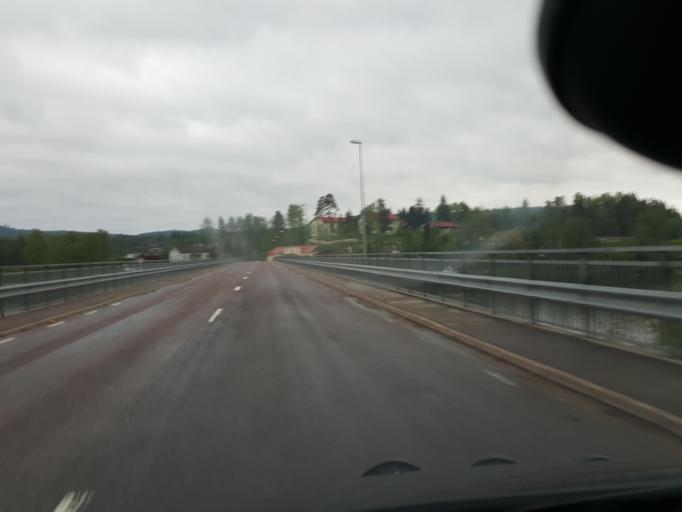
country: SE
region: Gaevleborg
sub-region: Ljusdals Kommun
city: Jaervsoe
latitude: 61.7121
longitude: 16.1813
